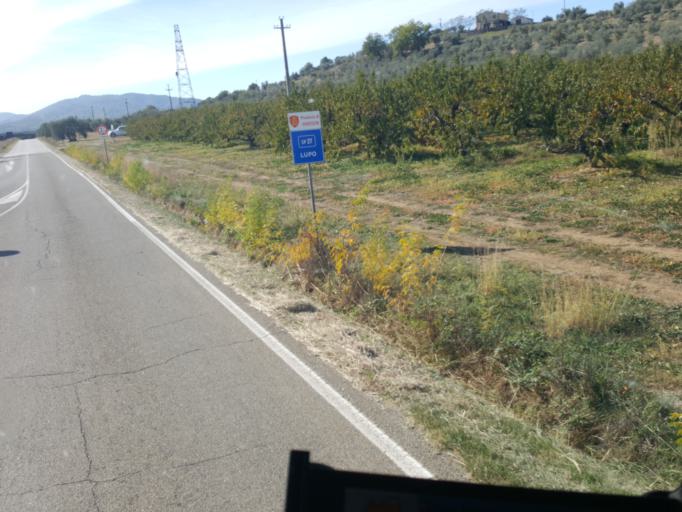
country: IT
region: Tuscany
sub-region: Provincia di Grosseto
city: Ribolla
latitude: 42.9167
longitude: 11.0213
